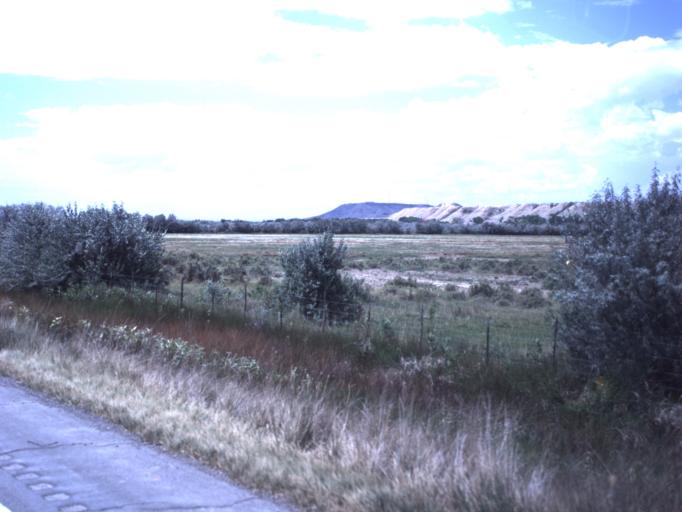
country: US
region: Utah
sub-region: Duchesne County
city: Roosevelt
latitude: 40.1591
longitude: -110.1712
